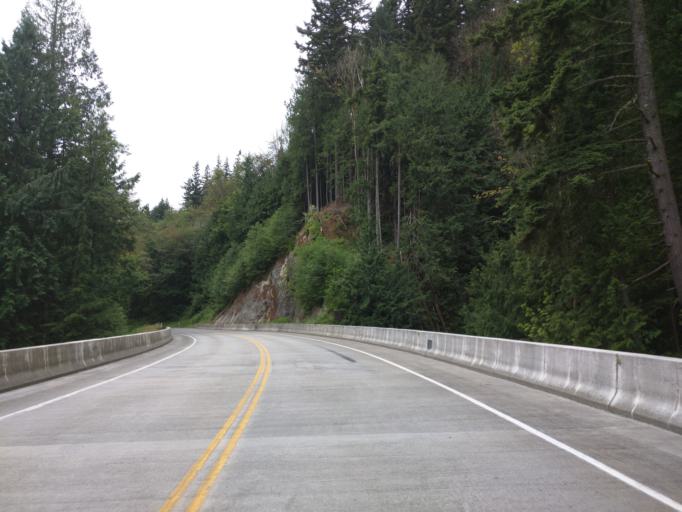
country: US
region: Washington
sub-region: Whatcom County
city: Sudden Valley
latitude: 48.6946
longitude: -122.3146
